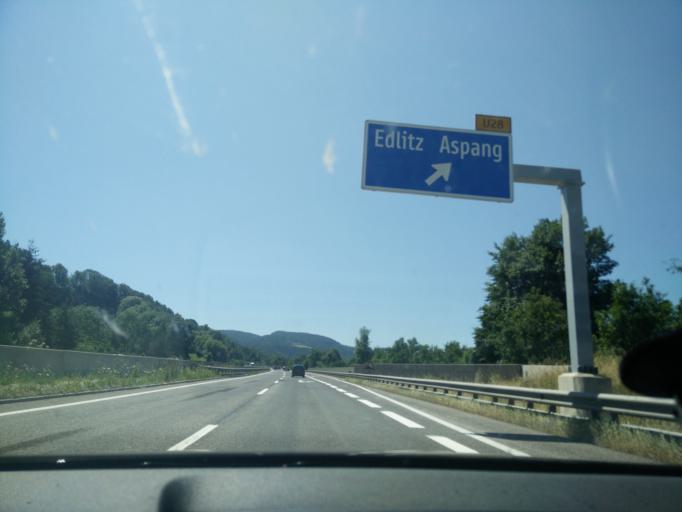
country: AT
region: Lower Austria
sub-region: Politischer Bezirk Neunkirchen
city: Grimmenstein
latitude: 47.6149
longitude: 16.1291
